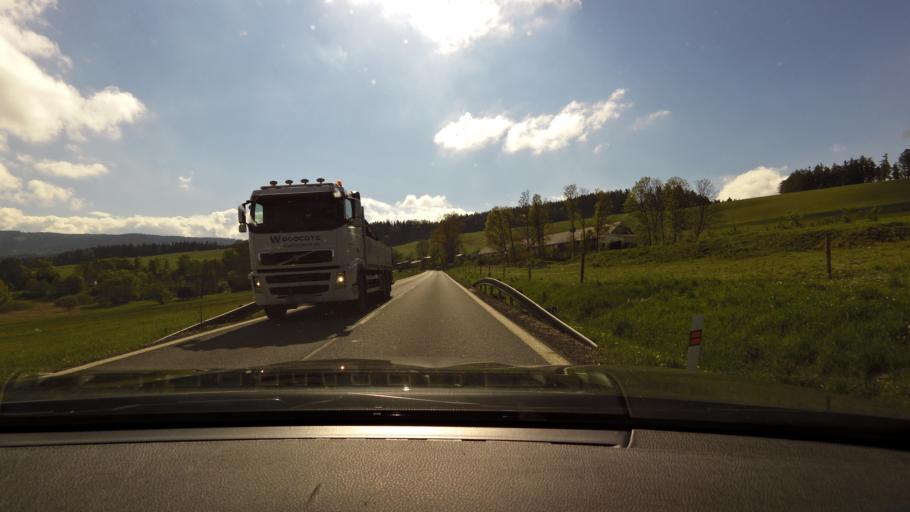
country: CZ
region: Plzensky
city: Strazov
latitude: 49.2482
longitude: 13.3011
